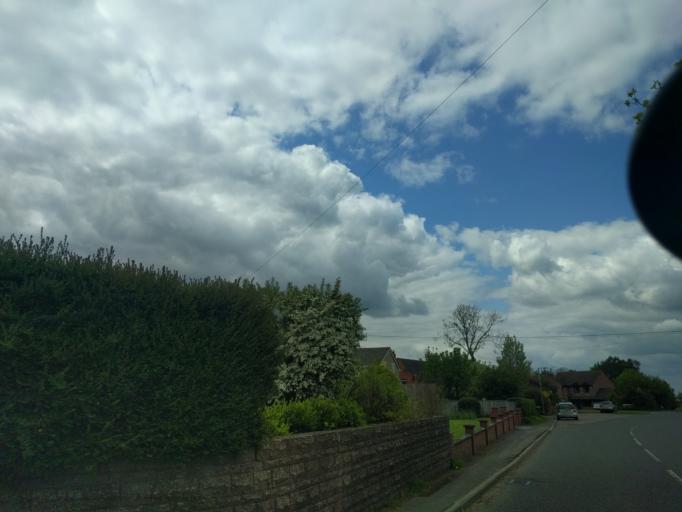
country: GB
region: England
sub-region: Wiltshire
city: Royal Wootton Bassett
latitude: 51.5389
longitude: -1.9111
